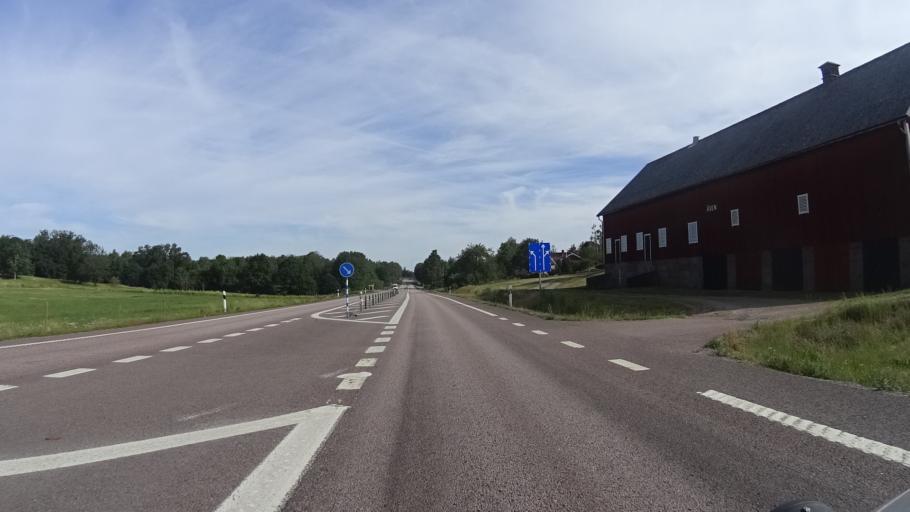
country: SE
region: Kalmar
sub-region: Oskarshamns Kommun
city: Oskarshamn
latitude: 57.4083
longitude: 16.4822
